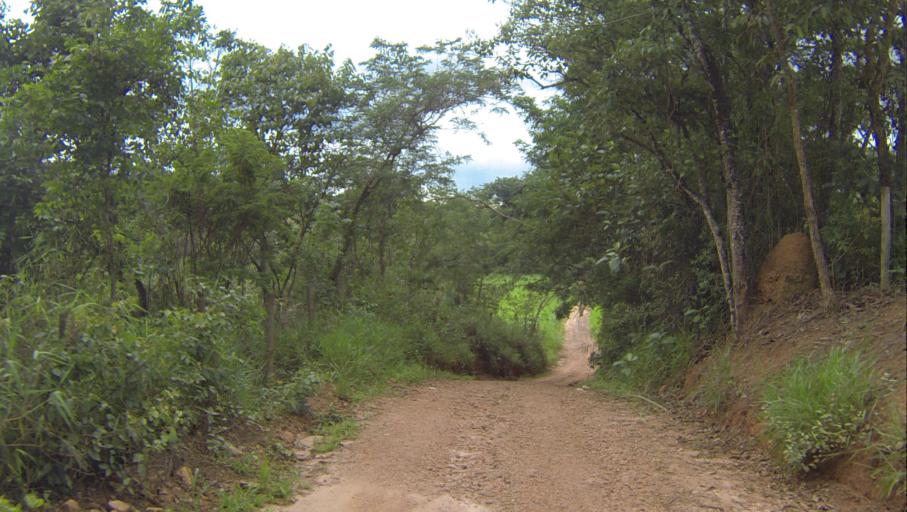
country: BR
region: Minas Gerais
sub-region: Brumadinho
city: Brumadinho
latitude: -20.1576
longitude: -44.1277
